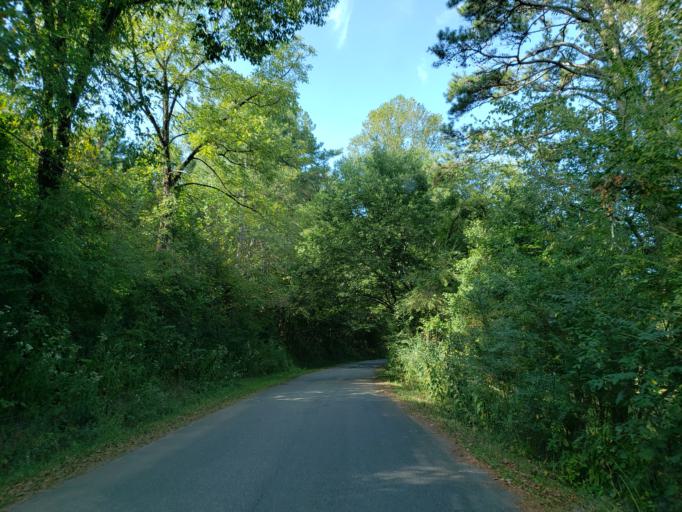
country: US
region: Georgia
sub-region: Gilmer County
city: Ellijay
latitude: 34.5773
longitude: -84.5102
